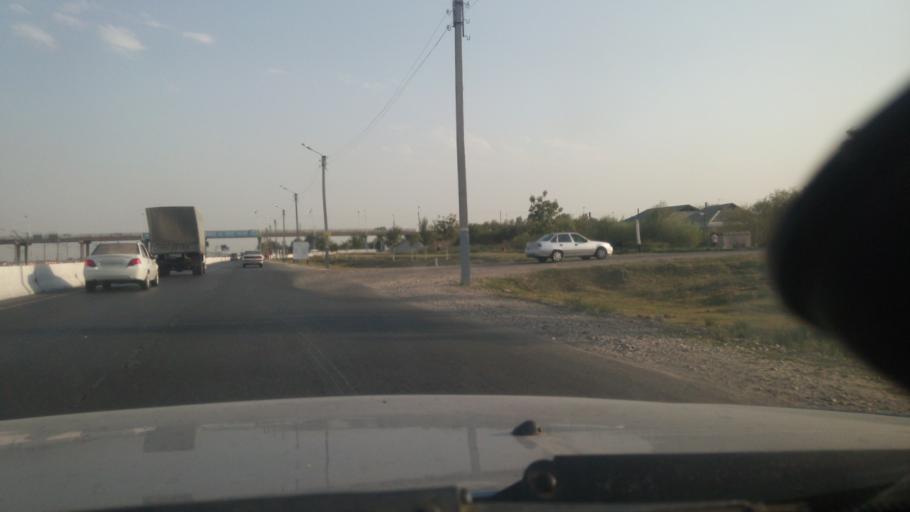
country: UZ
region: Sirdaryo
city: Guliston
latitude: 40.4767
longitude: 68.7698
